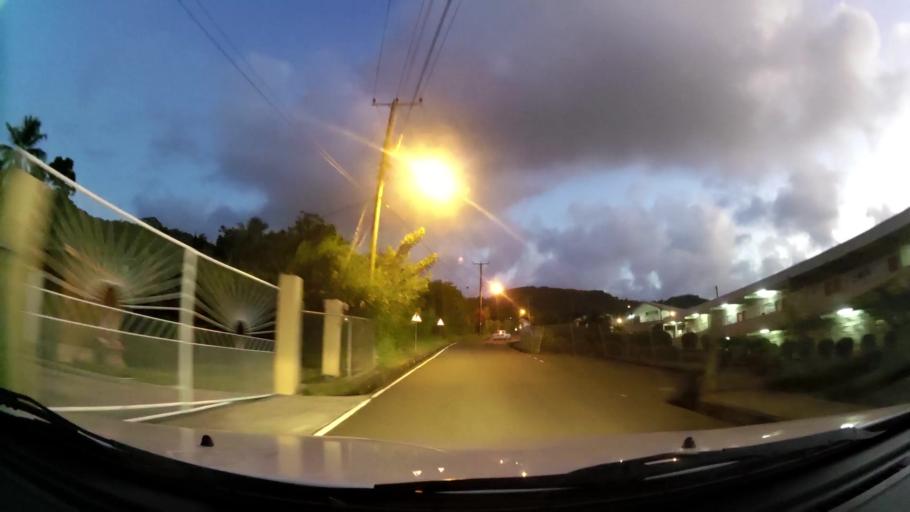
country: LC
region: Castries Quarter
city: Bisee
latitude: 14.0346
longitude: -60.9484
